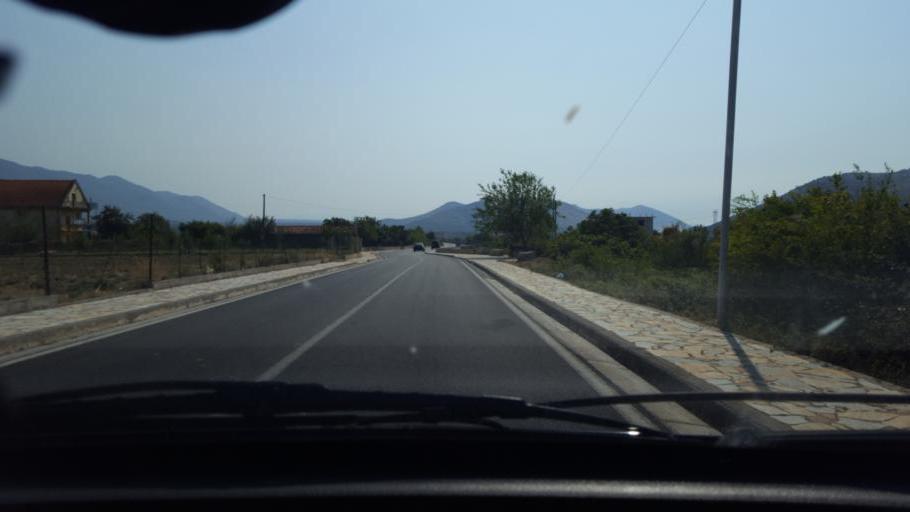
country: AL
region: Shkoder
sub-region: Rrethi i Malesia e Madhe
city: Hot
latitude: 42.3512
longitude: 19.4413
